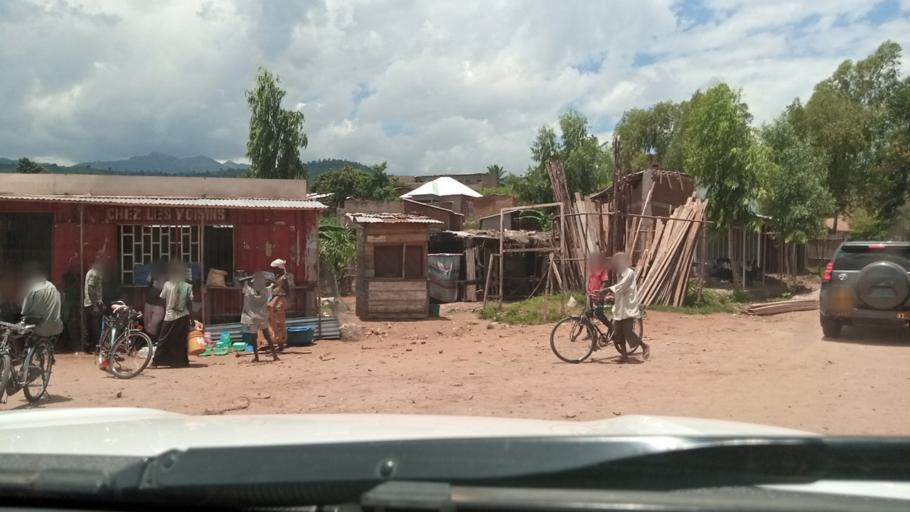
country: BI
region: Bujumbura Mairie
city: Bujumbura
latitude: -3.4807
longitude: 29.3534
